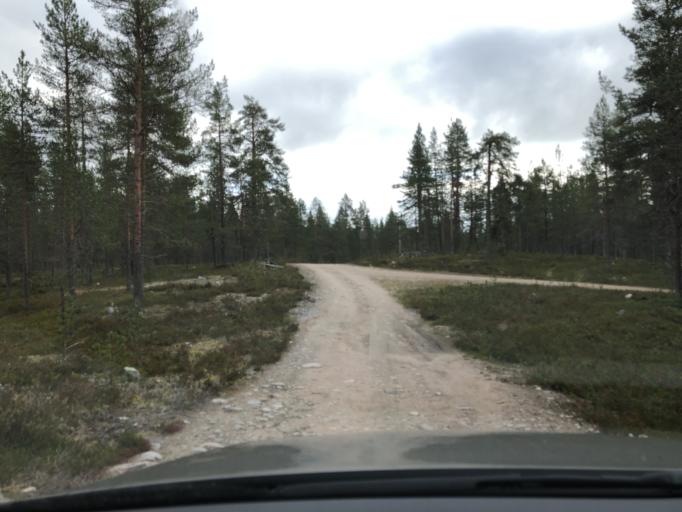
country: FI
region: Lapland
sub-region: Itae-Lappi
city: Posio
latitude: 66.0570
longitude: 27.8148
